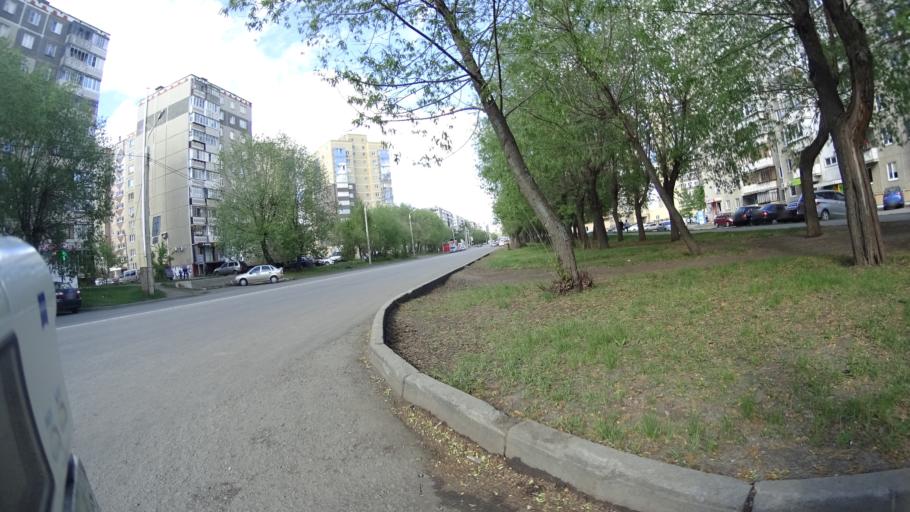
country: RU
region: Chelyabinsk
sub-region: Gorod Chelyabinsk
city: Chelyabinsk
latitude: 55.1768
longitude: 61.2962
